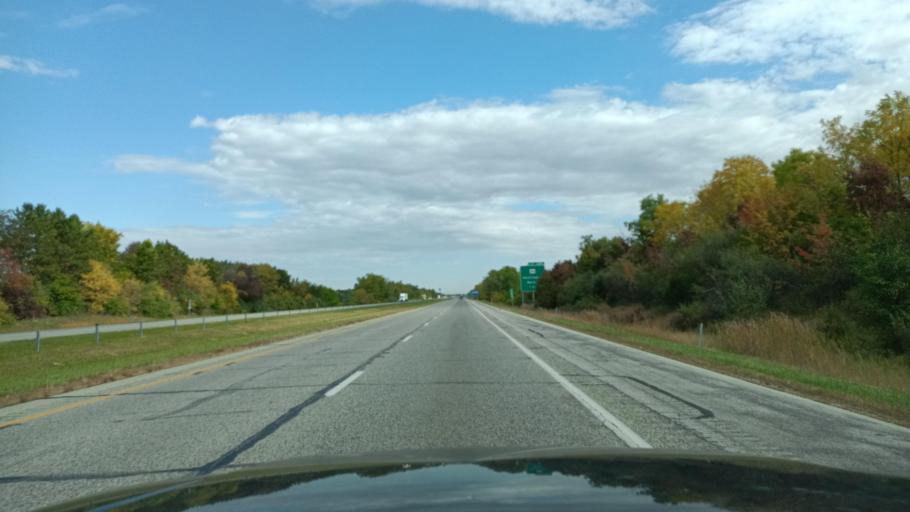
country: US
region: Indiana
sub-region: Huntington County
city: Markle
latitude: 40.8111
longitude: -85.3716
